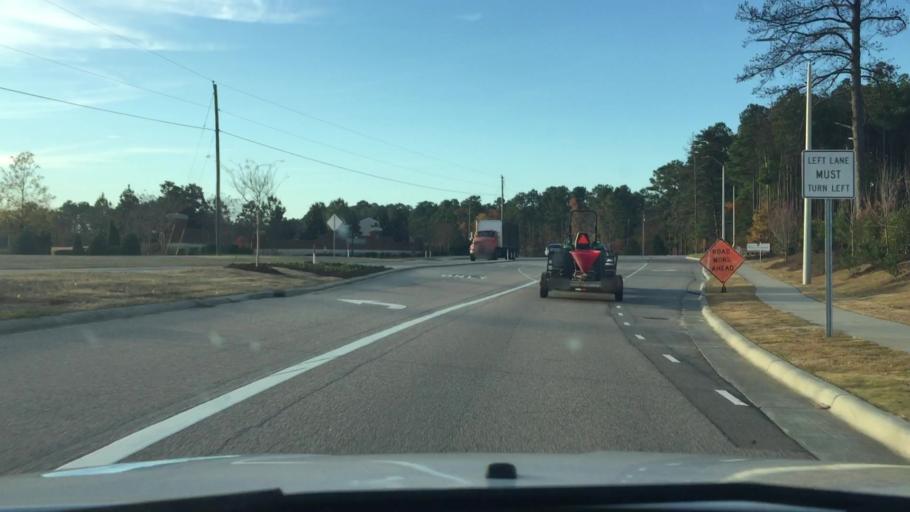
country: US
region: North Carolina
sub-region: Wake County
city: Green Level
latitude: 35.8437
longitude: -78.9122
